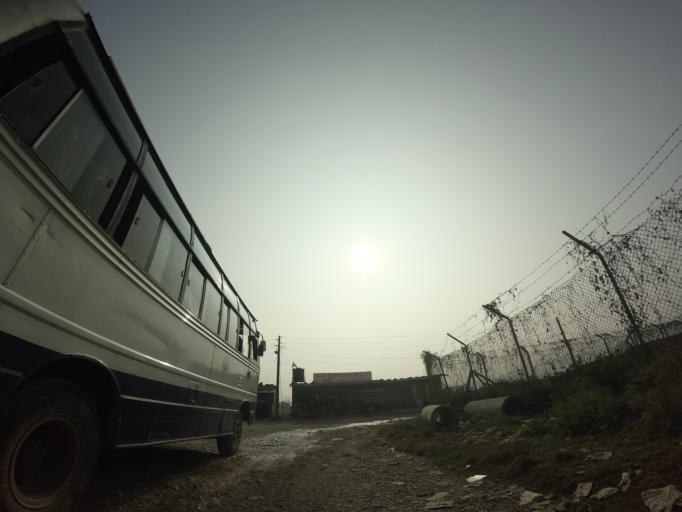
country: NP
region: Western Region
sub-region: Gandaki Zone
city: Pokhara
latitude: 28.2042
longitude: 83.9866
